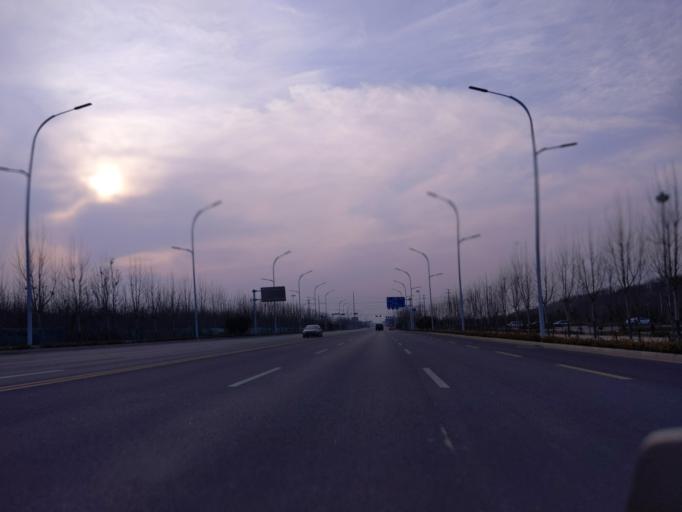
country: CN
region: Henan Sheng
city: Puyang
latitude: 35.8182
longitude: 115.0063
